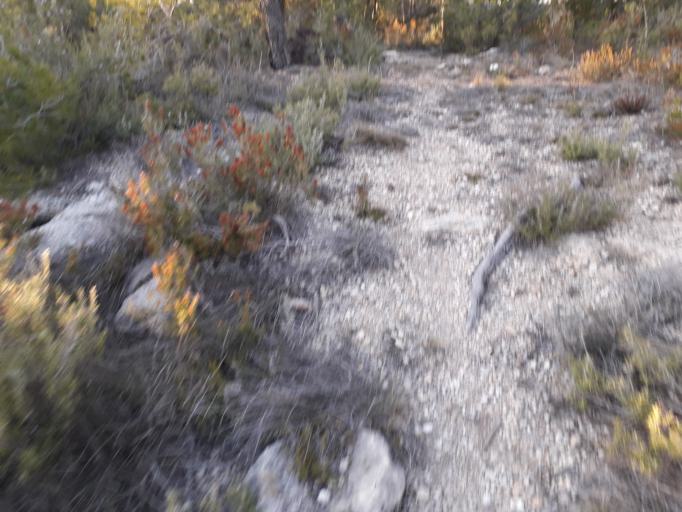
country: ES
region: Catalonia
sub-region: Provincia de Barcelona
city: Jorba
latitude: 41.6158
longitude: 1.5752
